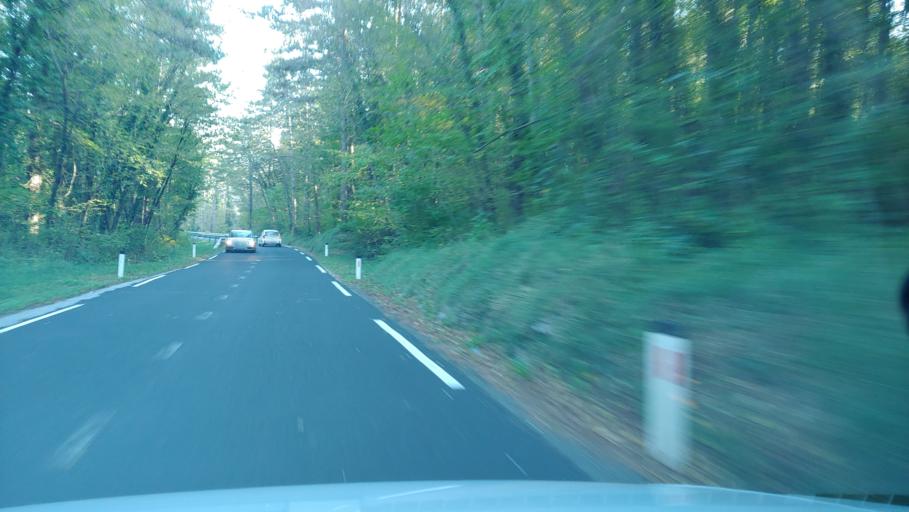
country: SI
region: Ajdovscina
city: Ajdovscina
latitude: 45.8122
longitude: 13.8545
